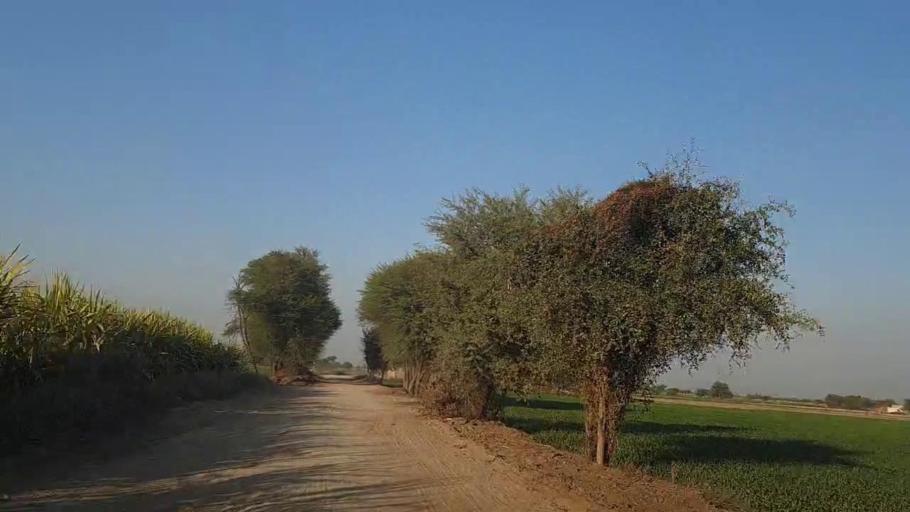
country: PK
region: Sindh
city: Sakrand
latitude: 26.2995
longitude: 68.1261
